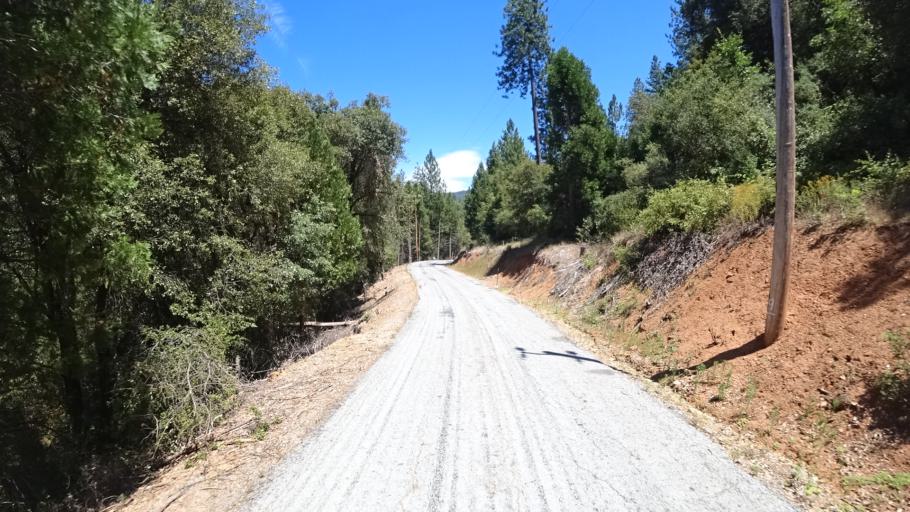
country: US
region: California
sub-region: Calaveras County
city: Forest Meadows
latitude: 38.2166
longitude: -120.4411
